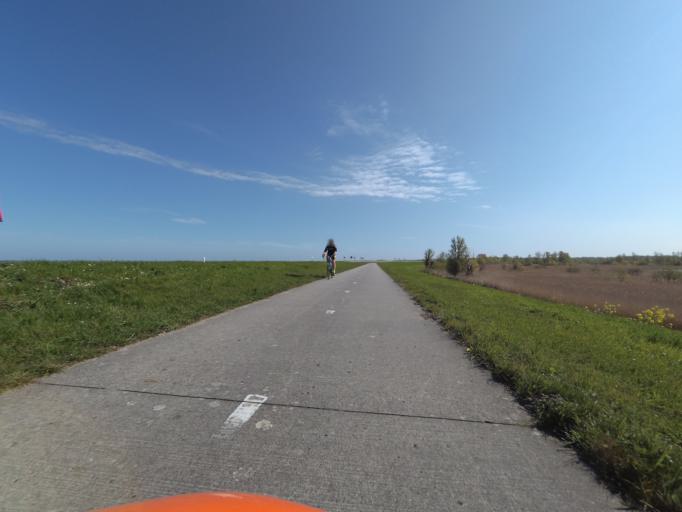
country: NL
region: Flevoland
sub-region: Gemeente Almere
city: Almere Stad
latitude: 52.4148
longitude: 5.2041
